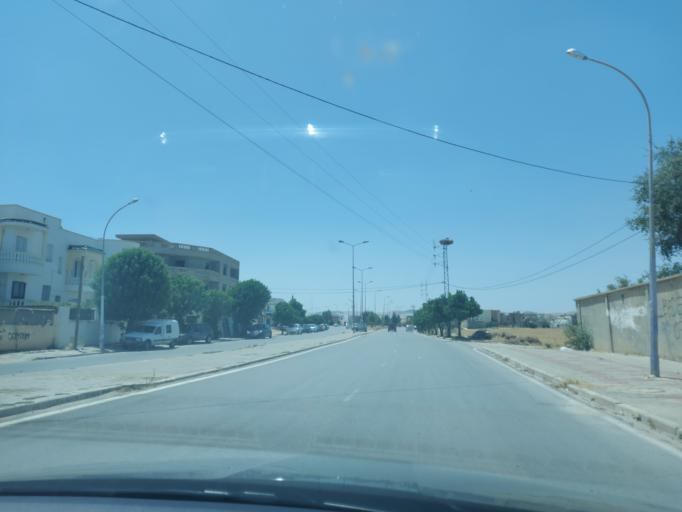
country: TN
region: Silyanah
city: Siliana
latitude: 36.0853
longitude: 9.3584
